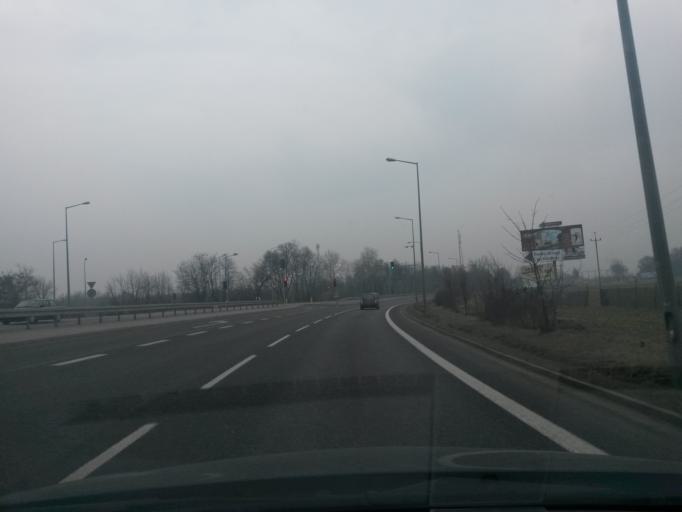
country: PL
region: Masovian Voivodeship
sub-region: Powiat legionowski
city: Bialobrzegi
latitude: 52.4711
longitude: 21.0293
